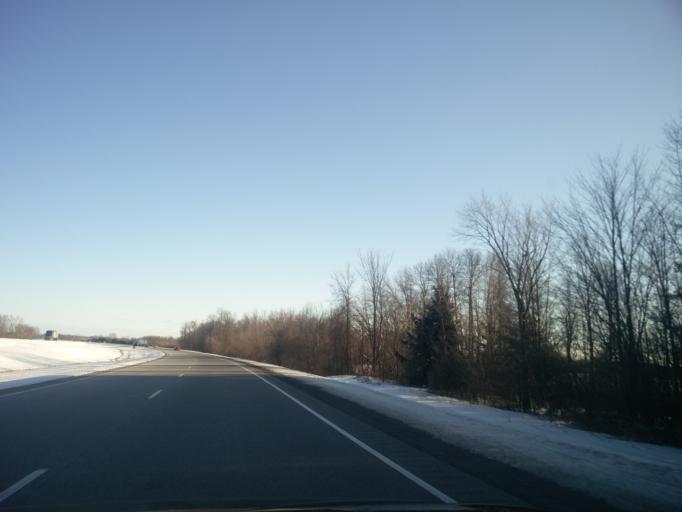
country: CA
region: Ontario
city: Prescott
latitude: 45.0127
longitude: -75.6276
